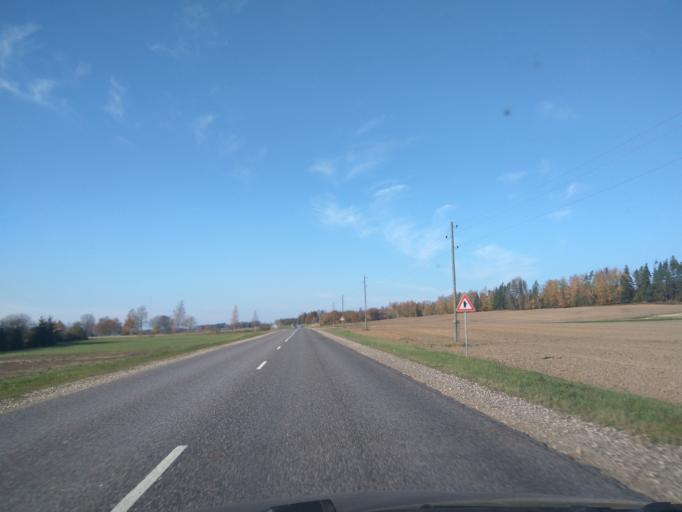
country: LV
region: Kuldigas Rajons
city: Kuldiga
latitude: 57.0214
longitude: 21.8681
